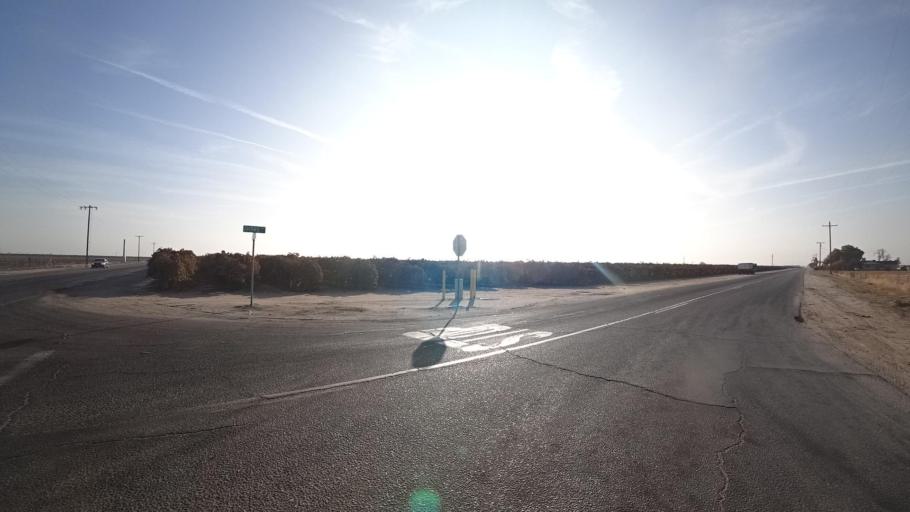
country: US
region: California
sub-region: Kern County
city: Delano
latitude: 35.7904
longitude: -119.1875
